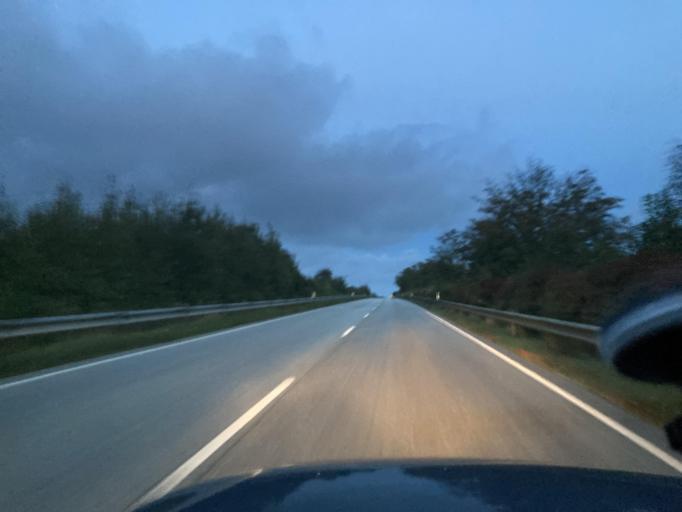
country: DE
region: Schleswig-Holstein
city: Tonning
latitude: 54.3247
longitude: 8.9320
